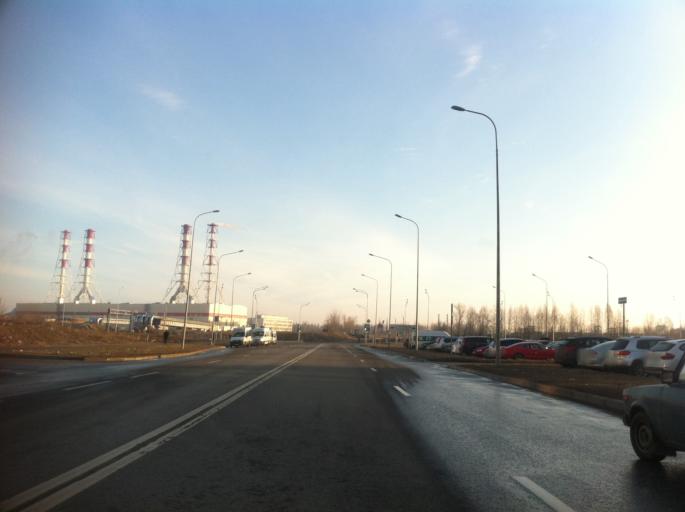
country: RU
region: St.-Petersburg
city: Uritsk
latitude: 59.8639
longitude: 30.1820
